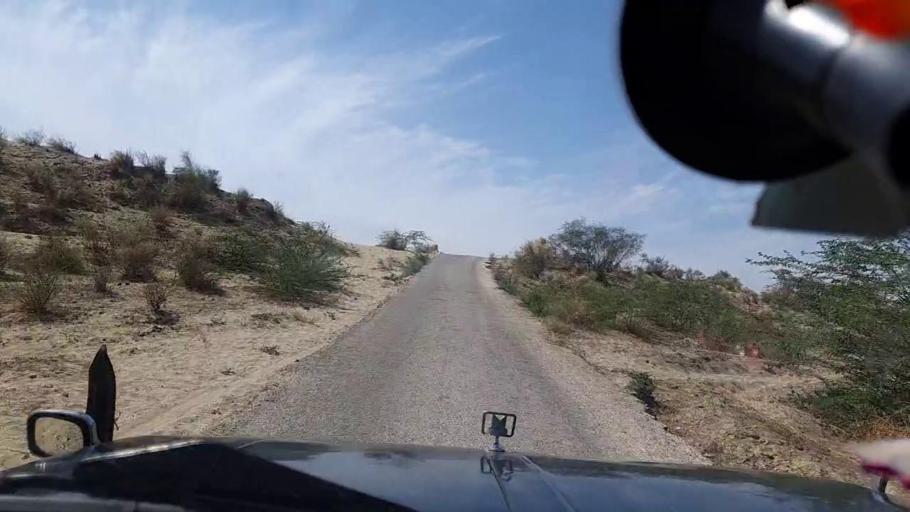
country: PK
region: Sindh
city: Diplo
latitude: 24.4111
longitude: 69.5853
